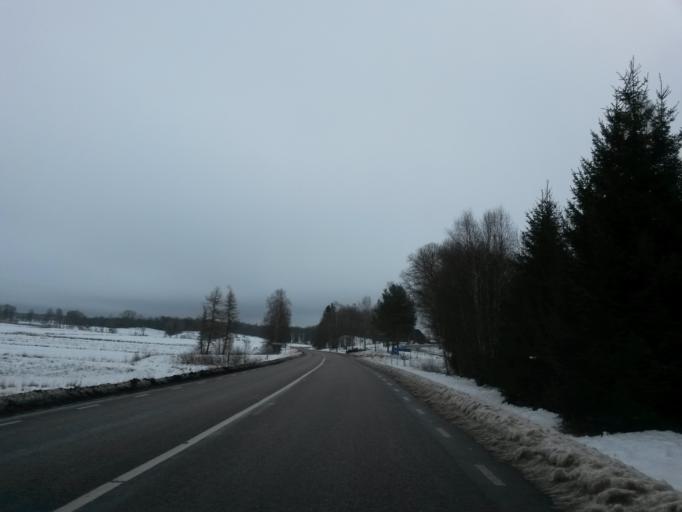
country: SE
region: Vaestra Goetaland
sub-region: Herrljunga Kommun
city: Herrljunga
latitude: 57.9486
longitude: 13.1849
